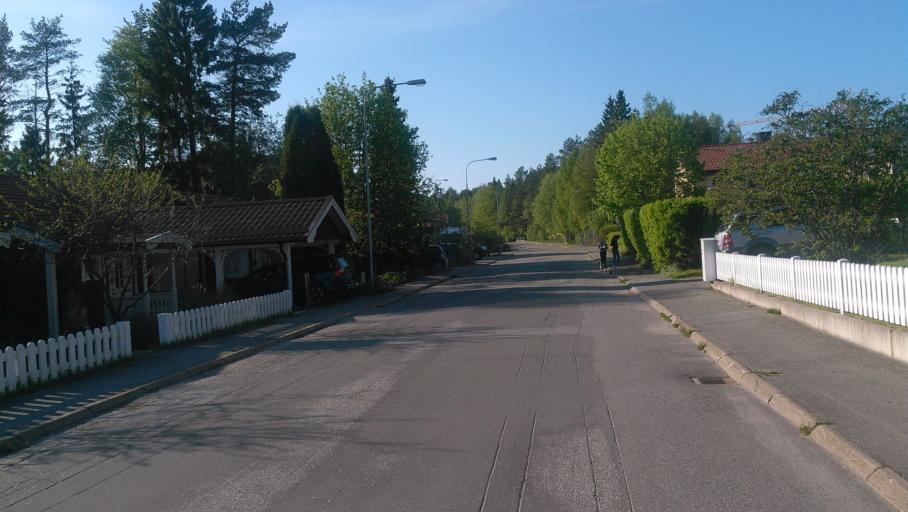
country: SE
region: Vaesterbotten
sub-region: Umea Kommun
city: Umea
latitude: 63.8093
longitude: 20.3053
